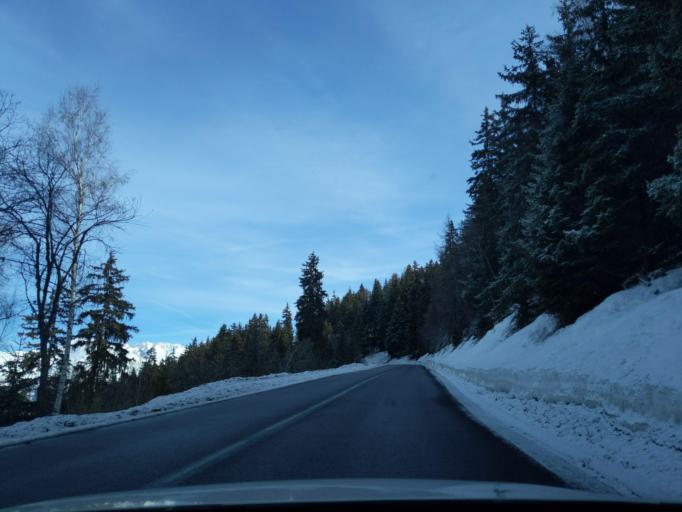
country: FR
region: Rhone-Alpes
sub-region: Departement de la Savoie
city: Bourg-Saint-Maurice
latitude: 45.5865
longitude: 6.7837
